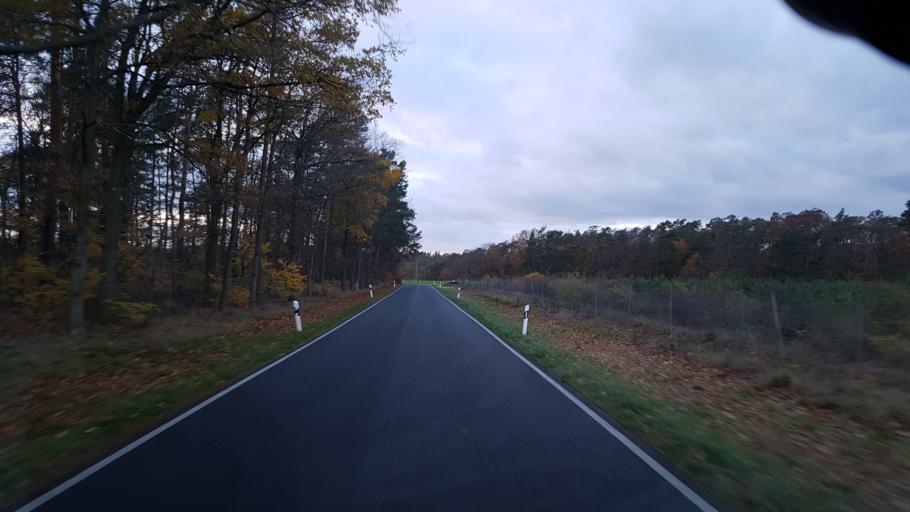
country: DE
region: Brandenburg
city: Tettau
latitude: 51.4245
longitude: 13.7434
